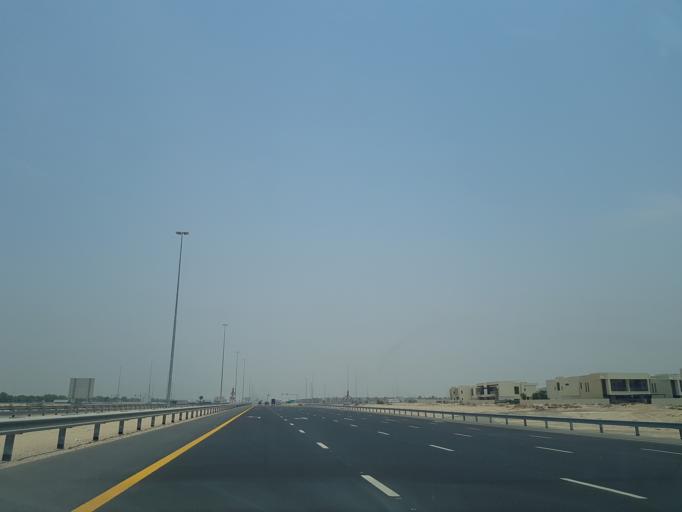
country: AE
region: Dubai
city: Dubai
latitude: 25.0329
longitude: 55.2558
